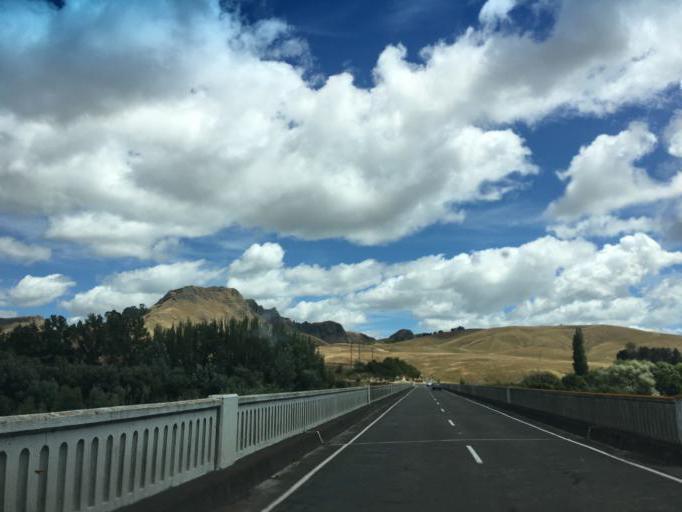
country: NZ
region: Hawke's Bay
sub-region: Hastings District
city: Hastings
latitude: -39.7166
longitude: 176.9287
